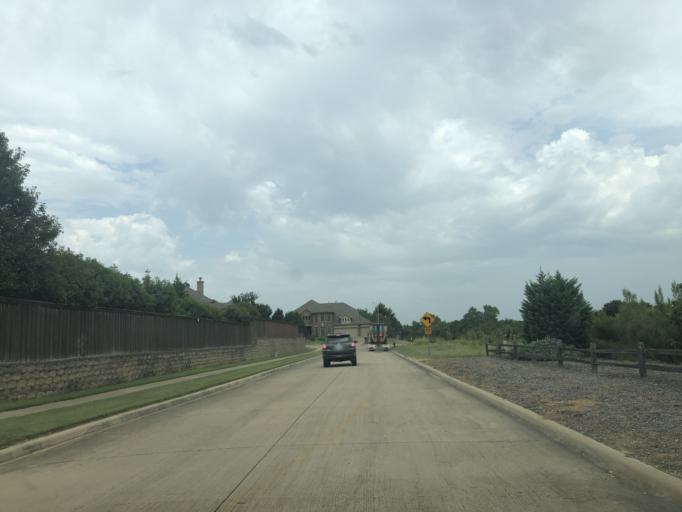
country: US
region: Texas
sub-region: Dallas County
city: Grand Prairie
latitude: 32.7668
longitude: -97.0403
